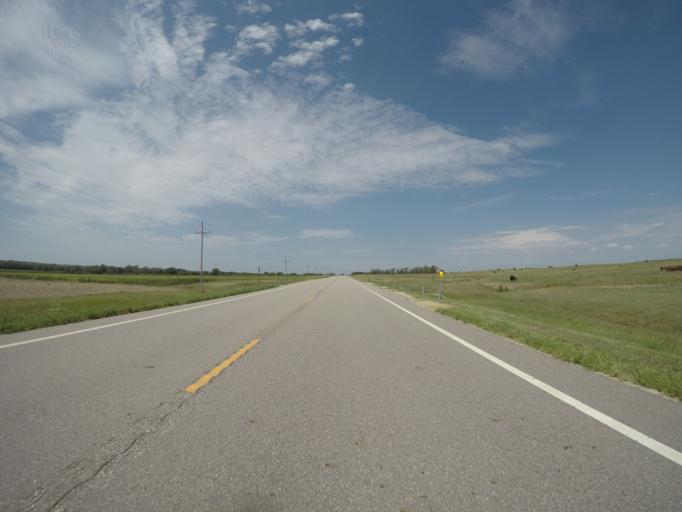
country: US
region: Kansas
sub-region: Rooks County
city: Stockton
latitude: 39.4444
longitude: -99.1786
